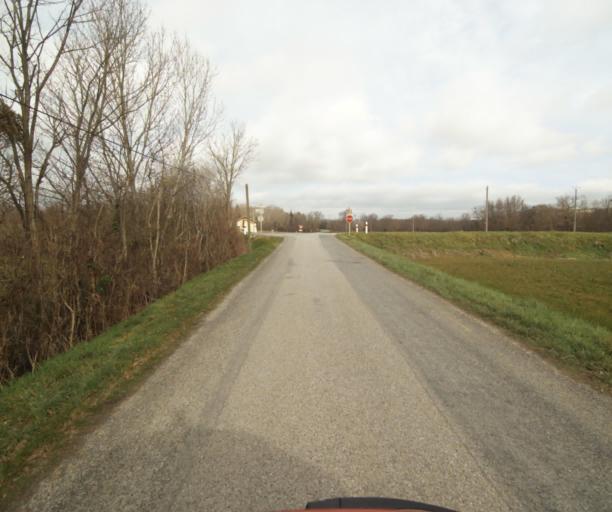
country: FR
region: Midi-Pyrenees
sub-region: Departement de l'Ariege
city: Pamiers
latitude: 43.1073
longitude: 1.5477
